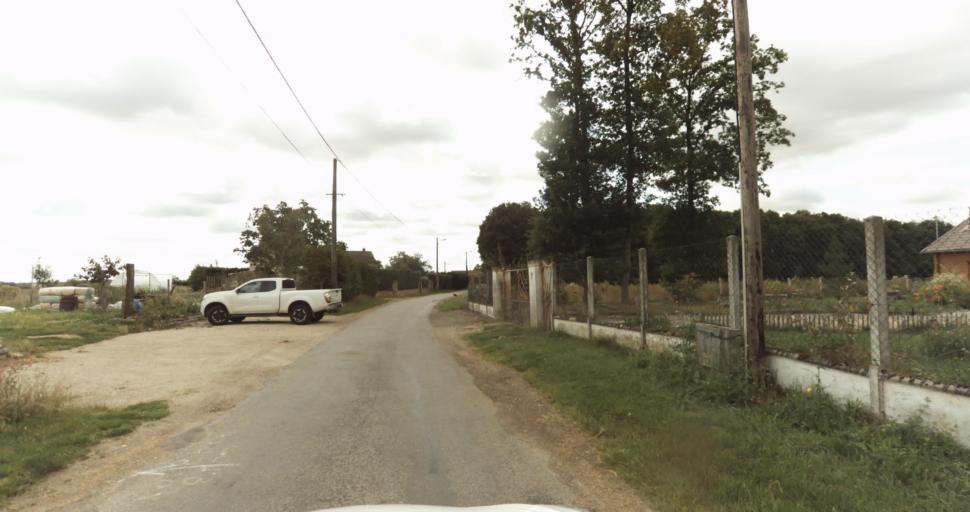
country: FR
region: Haute-Normandie
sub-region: Departement de l'Eure
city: Nonancourt
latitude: 48.7899
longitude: 1.1445
